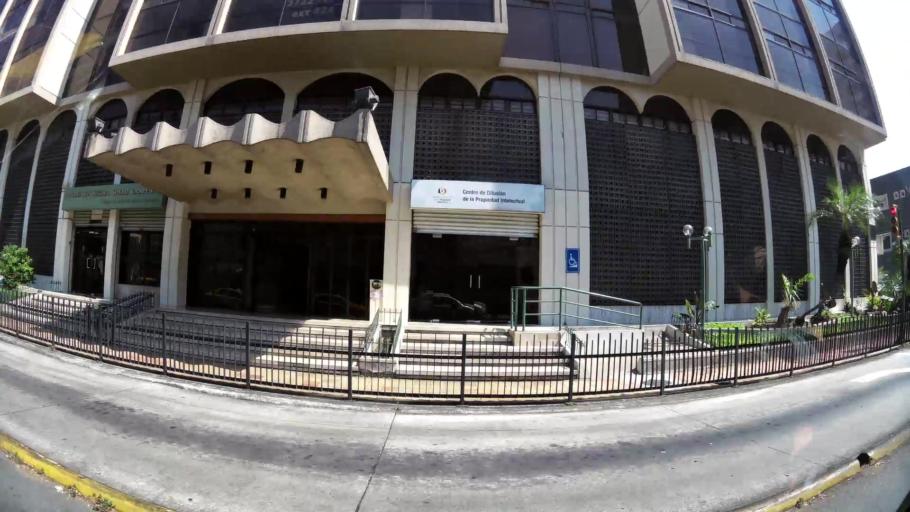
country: EC
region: Guayas
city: Guayaquil
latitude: -2.1869
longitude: -79.8954
